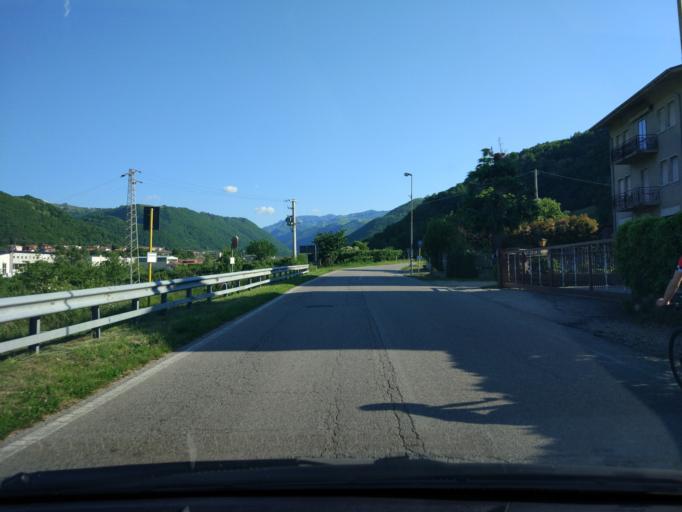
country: IT
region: Veneto
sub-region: Provincia di Verona
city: Badia Calavena
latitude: 45.5511
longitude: 11.1554
